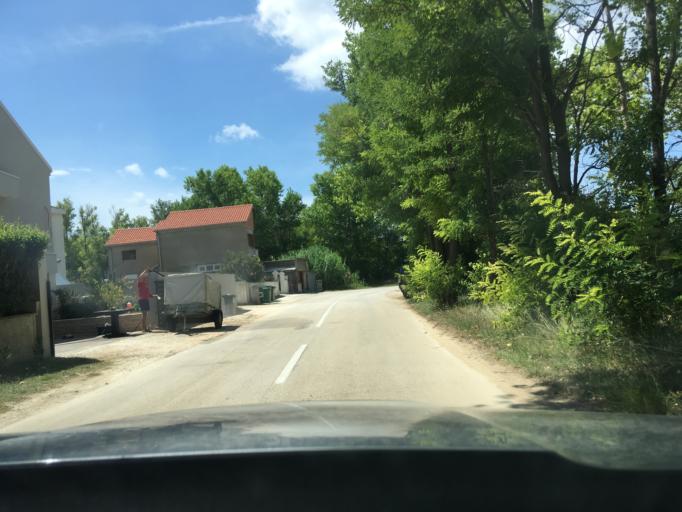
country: HR
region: Zadarska
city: Nin
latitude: 44.2512
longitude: 15.1552
